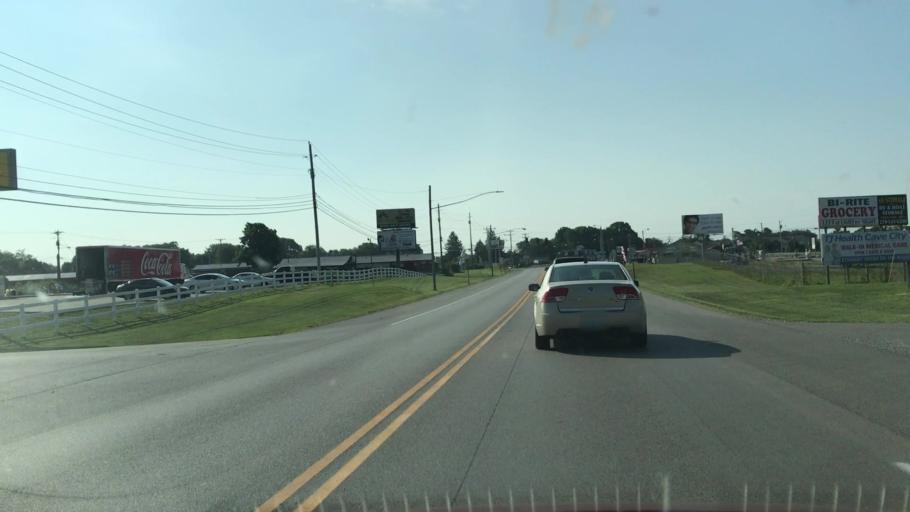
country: US
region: Kentucky
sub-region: Barren County
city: Cave City
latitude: 37.1296
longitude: -85.9649
